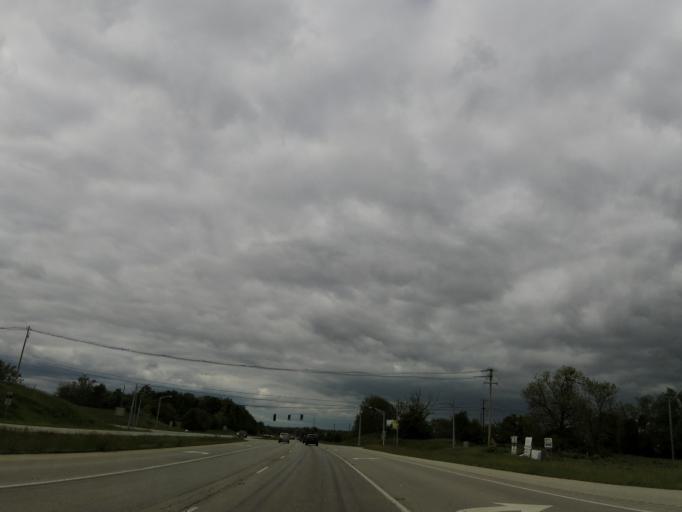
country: US
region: Kentucky
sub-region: Scott County
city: Georgetown
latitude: 38.1972
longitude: -84.5390
